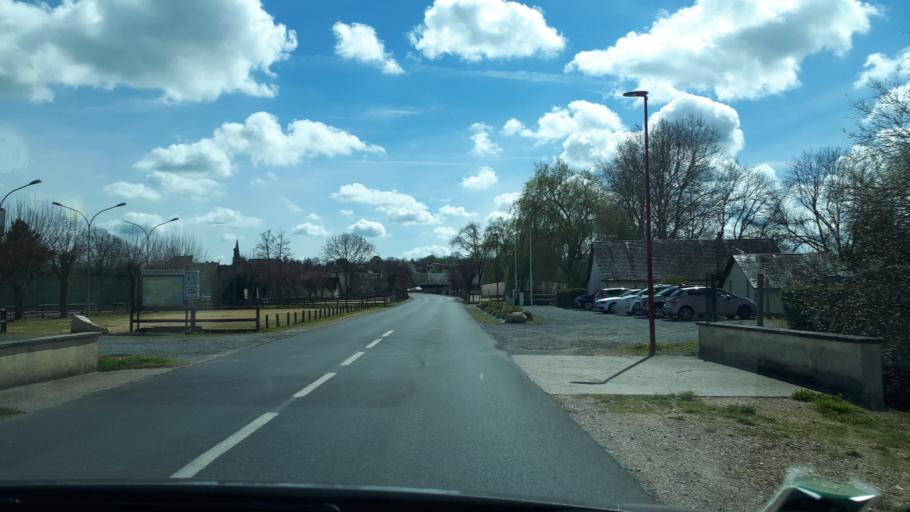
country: FR
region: Centre
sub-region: Departement du Loir-et-Cher
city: Savigny-sur-Braye
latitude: 47.8810
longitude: 0.8018
